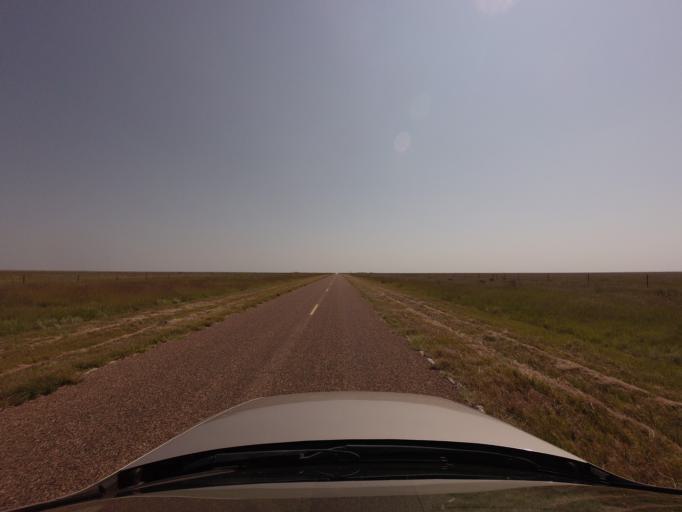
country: US
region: New Mexico
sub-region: Curry County
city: Cannon Air Force Base
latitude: 34.6333
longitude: -103.4446
